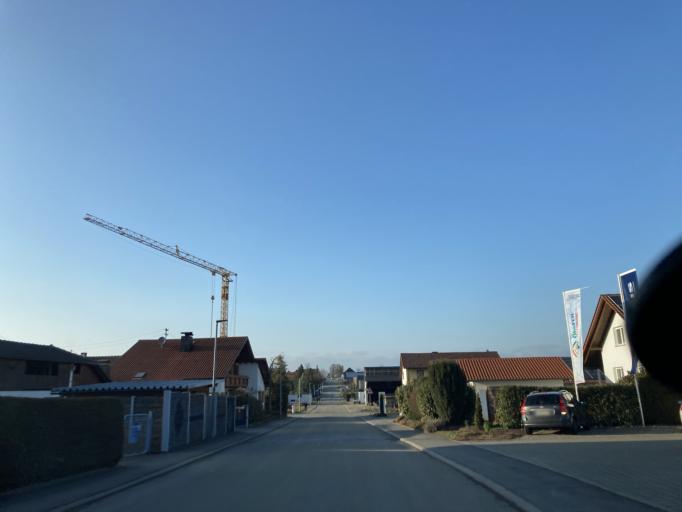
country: DE
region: Baden-Wuerttemberg
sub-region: Tuebingen Region
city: Hirrlingen
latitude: 48.4107
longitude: 8.8946
